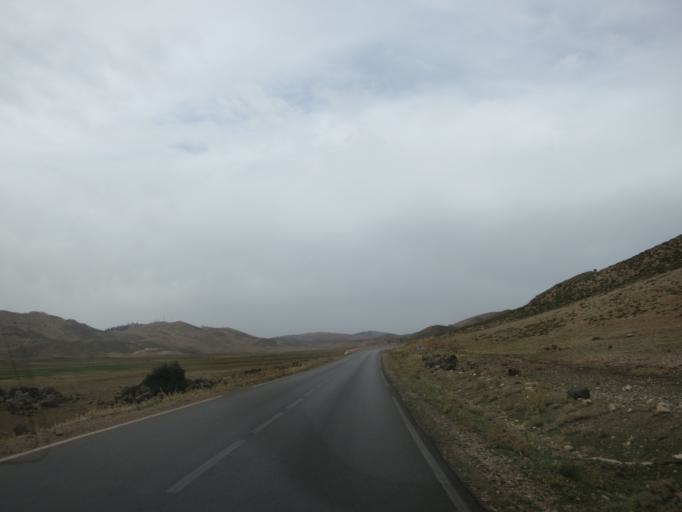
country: MA
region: Meknes-Tafilalet
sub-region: Khenifra
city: Itzer
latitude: 33.0746
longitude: -5.0211
